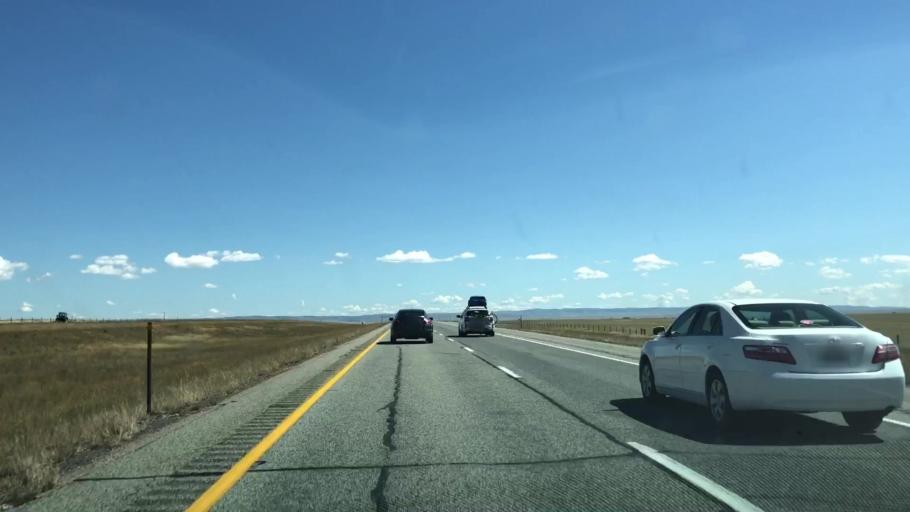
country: US
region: Wyoming
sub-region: Albany County
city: Laramie
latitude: 41.4350
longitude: -105.9066
